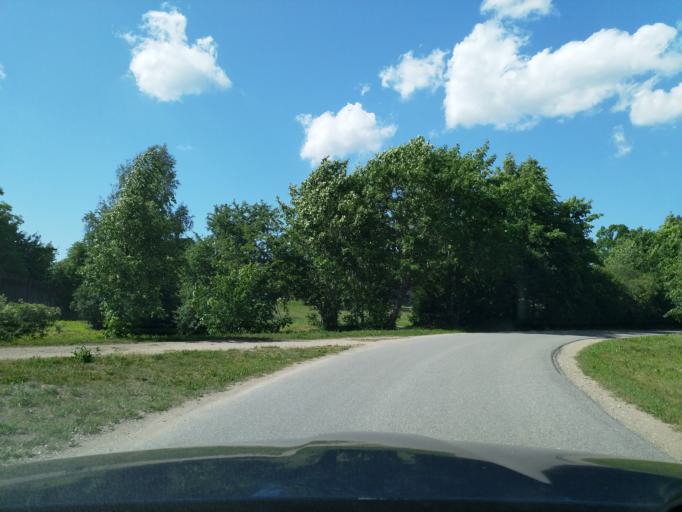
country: LV
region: Alsunga
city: Alsunga
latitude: 56.9772
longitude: 21.5654
